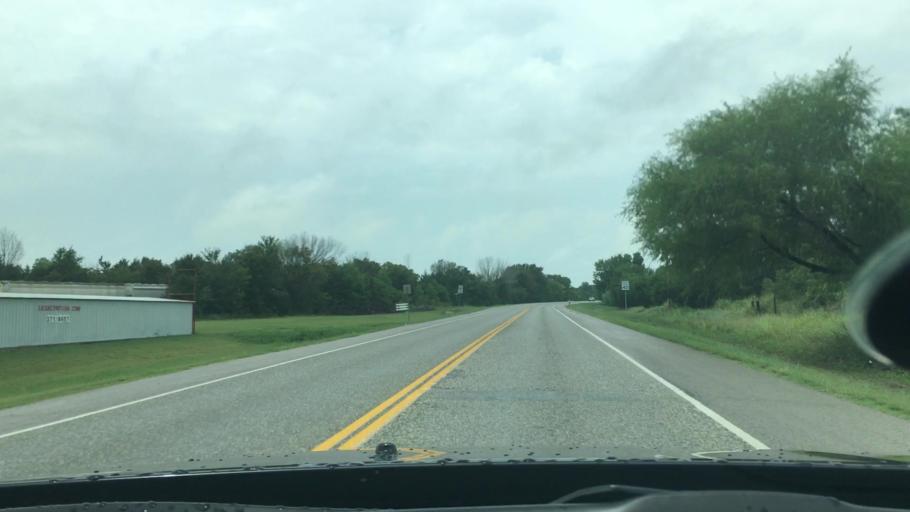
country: US
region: Oklahoma
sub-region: Johnston County
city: Tishomingo
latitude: 34.2471
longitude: -96.7561
